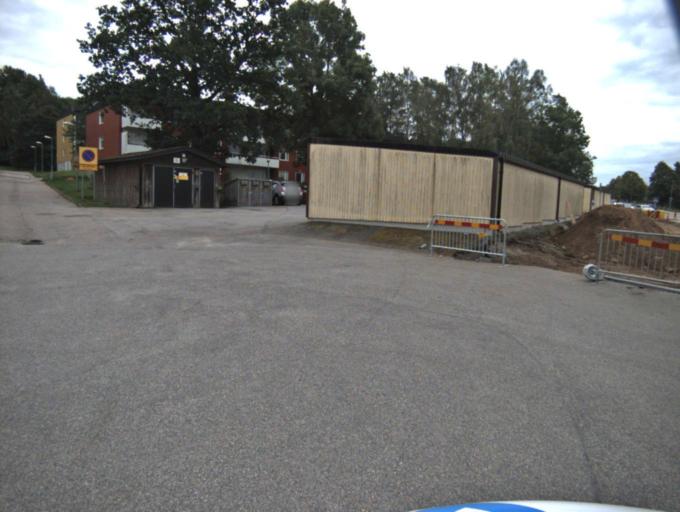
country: SE
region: Vaestra Goetaland
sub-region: Ulricehamns Kommun
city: Ulricehamn
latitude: 57.7935
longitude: 13.4249
